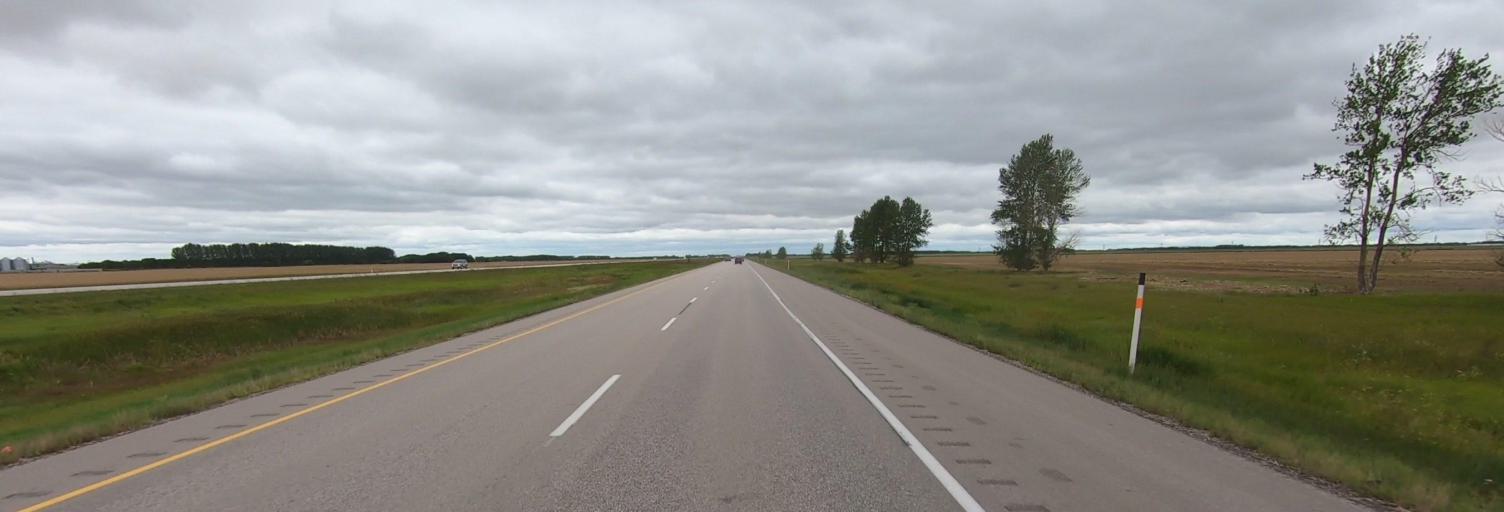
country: CA
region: Manitoba
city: Headingley
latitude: 49.9202
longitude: -97.8282
